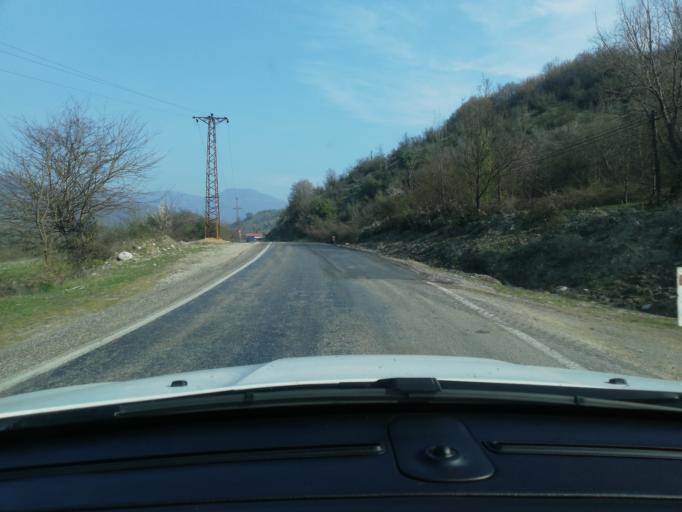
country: TR
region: Karabuk
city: Yenice
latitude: 41.2337
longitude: 32.3607
